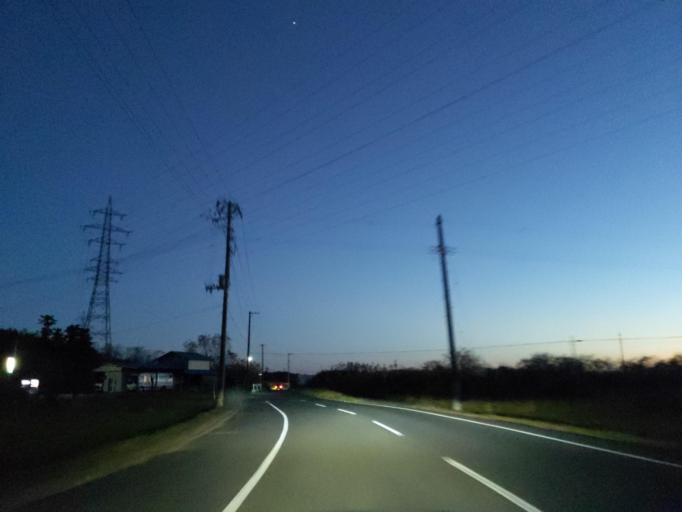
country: JP
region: Fukushima
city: Sukagawa
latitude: 37.3214
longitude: 140.3909
